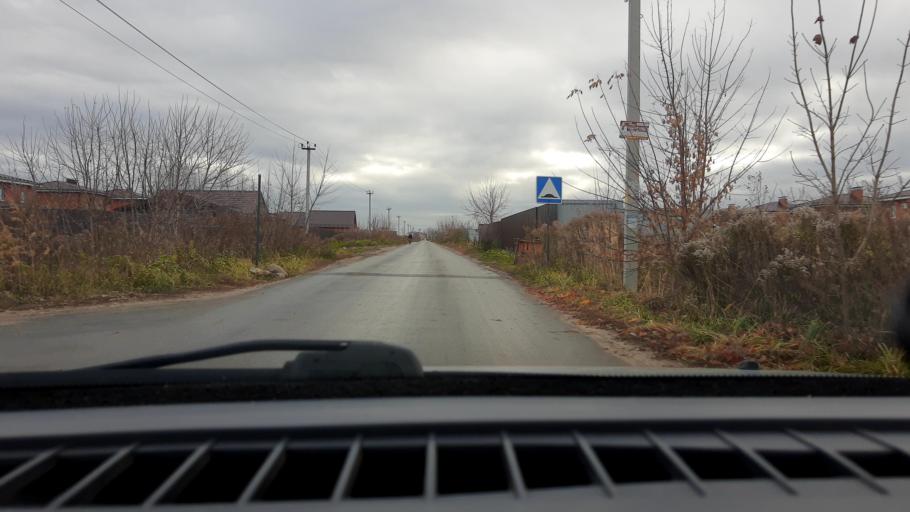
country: RU
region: Nizjnij Novgorod
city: Afonino
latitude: 56.2053
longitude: 44.1279
